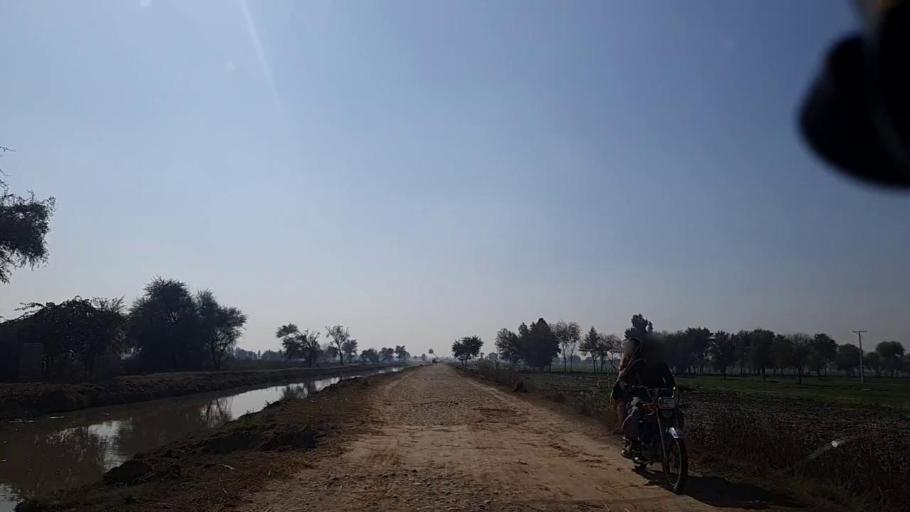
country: PK
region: Sindh
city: Khanpur
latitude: 27.8017
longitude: 69.4104
